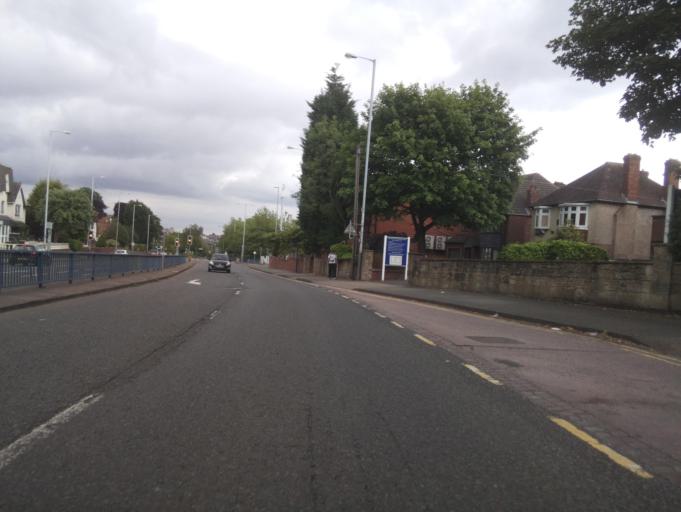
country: GB
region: England
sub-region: Wolverhampton
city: Wolverhampton
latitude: 52.5744
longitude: -2.1371
